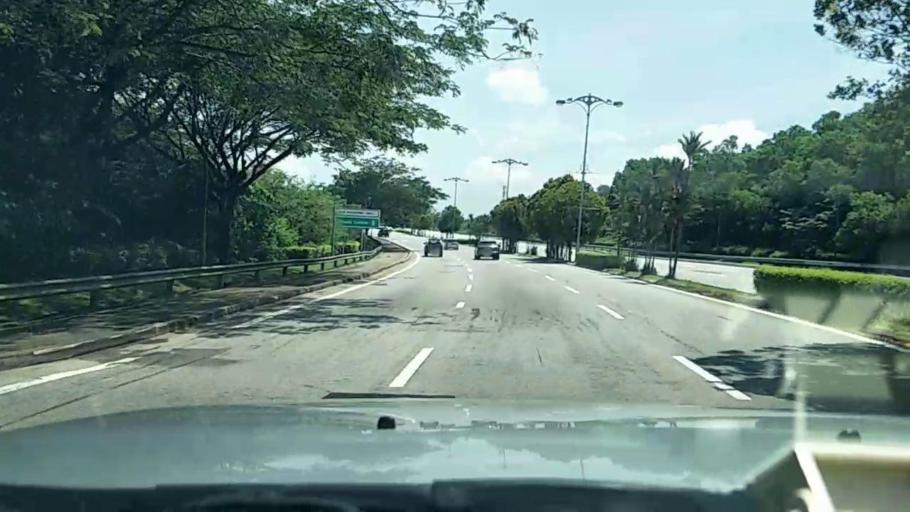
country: MY
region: Putrajaya
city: Putrajaya
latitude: 2.9455
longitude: 101.6689
